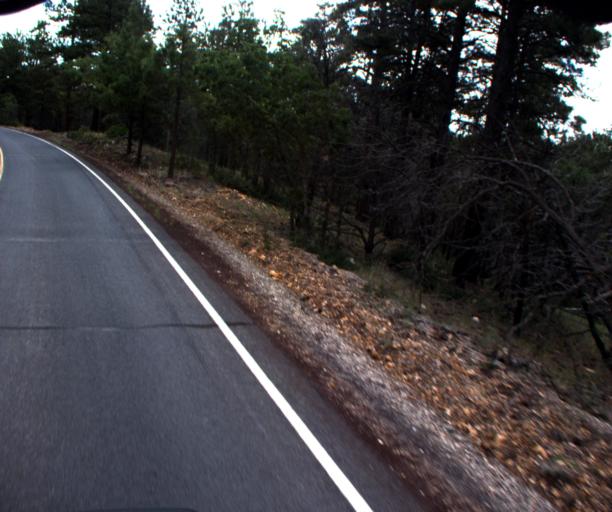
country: US
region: Arizona
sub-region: Coconino County
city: Grand Canyon
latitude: 35.9802
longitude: -111.9455
